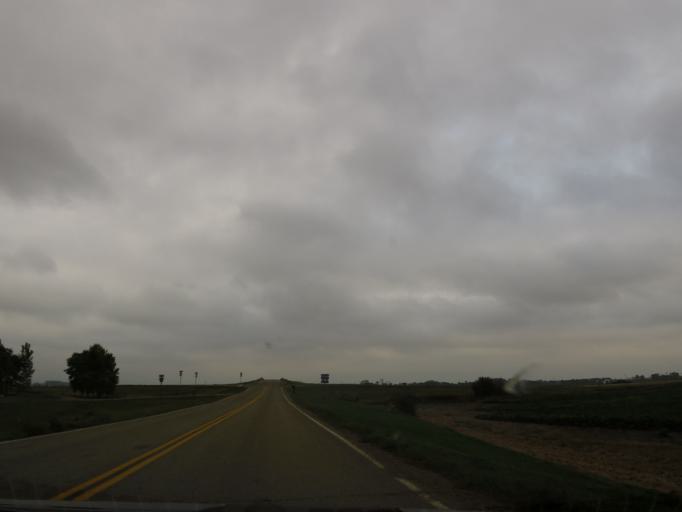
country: US
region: North Dakota
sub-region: Walsh County
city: Grafton
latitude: 48.4704
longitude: -97.1944
